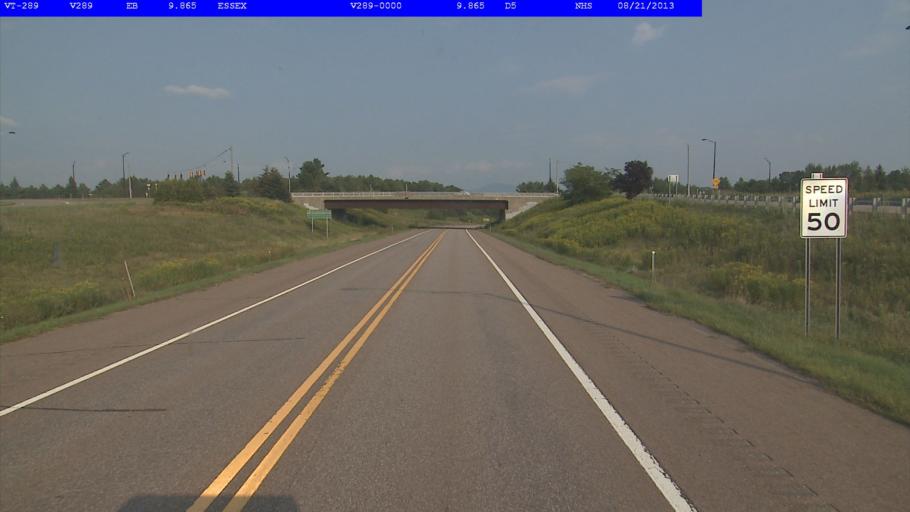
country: US
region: Vermont
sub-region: Chittenden County
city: Essex Junction
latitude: 44.5050
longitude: -73.0808
